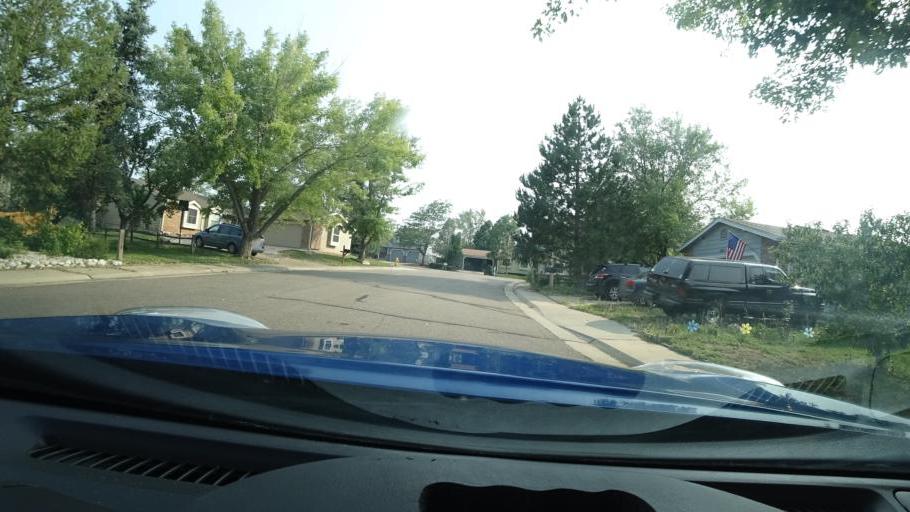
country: US
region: Colorado
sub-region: Adams County
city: Aurora
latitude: 39.6646
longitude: -104.7852
